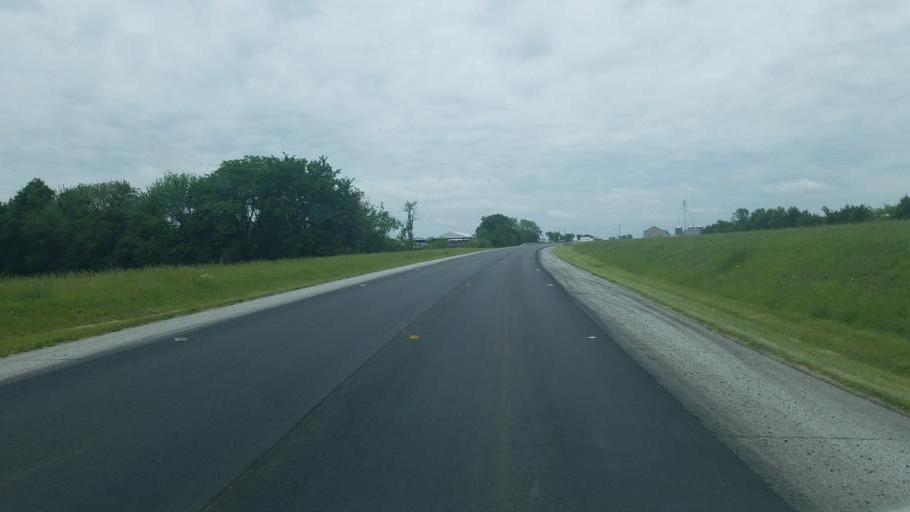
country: US
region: Missouri
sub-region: Morgan County
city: Versailles
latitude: 38.4448
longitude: -92.8336
